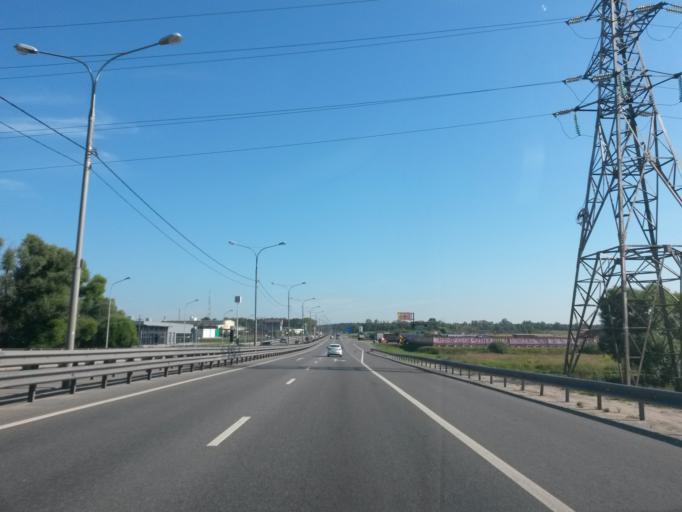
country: RU
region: Moskovskaya
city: Lesnyye Polyany
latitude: 55.9907
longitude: 37.8732
